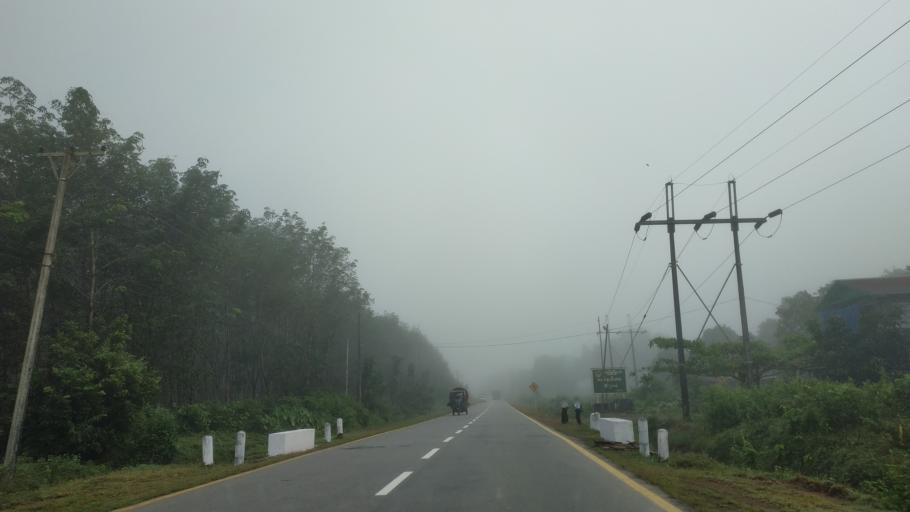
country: MM
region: Tanintharyi
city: Dawei
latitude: 14.1752
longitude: 98.2091
